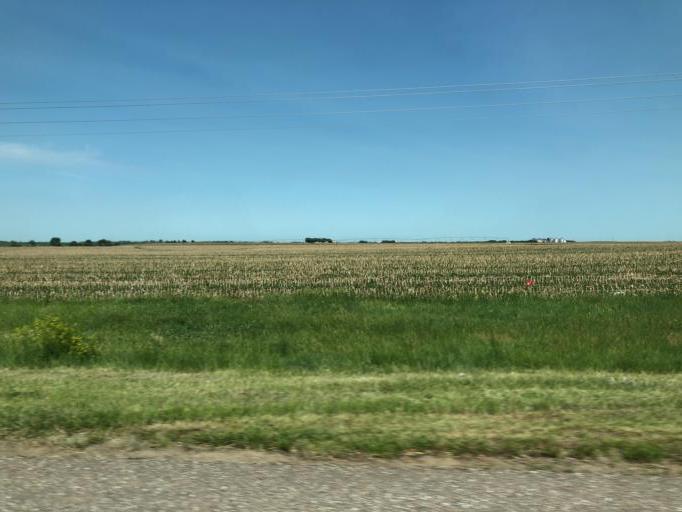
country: US
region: Nebraska
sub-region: Fillmore County
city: Geneva
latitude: 40.5712
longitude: -97.5956
